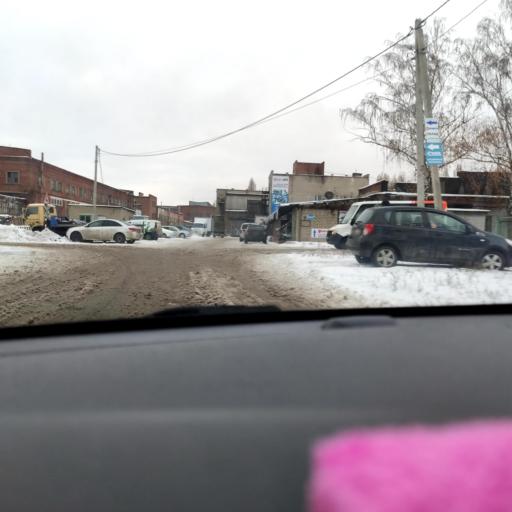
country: RU
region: Voronezj
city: Voronezh
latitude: 51.6834
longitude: 39.1639
